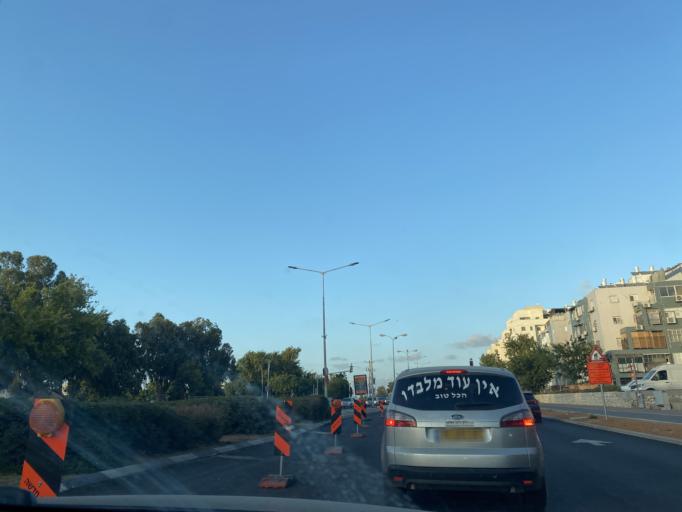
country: IL
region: Southern District
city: Ashdod
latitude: 31.8054
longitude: 34.6612
